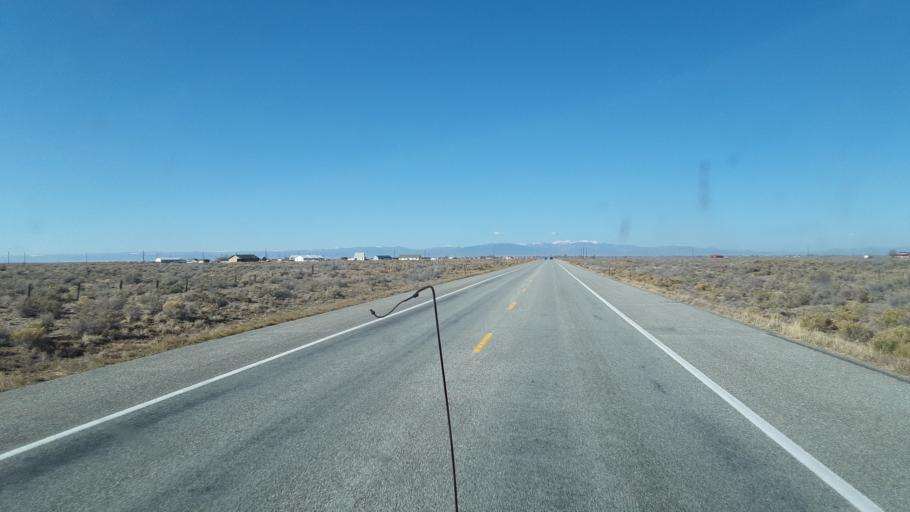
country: US
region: Colorado
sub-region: Alamosa County
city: Alamosa East
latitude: 37.4746
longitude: -105.6854
